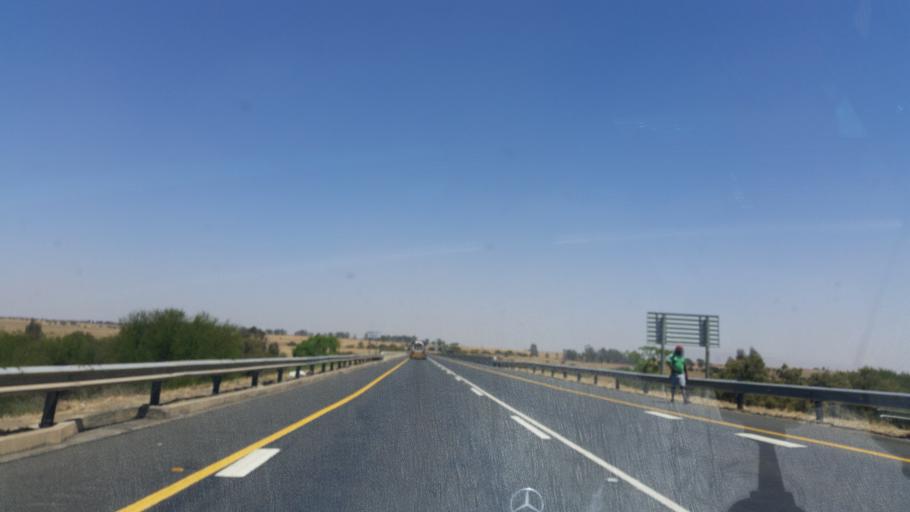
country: ZA
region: Orange Free State
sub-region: Lejweleputswa District Municipality
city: Winburg
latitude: -28.6307
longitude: 26.9050
